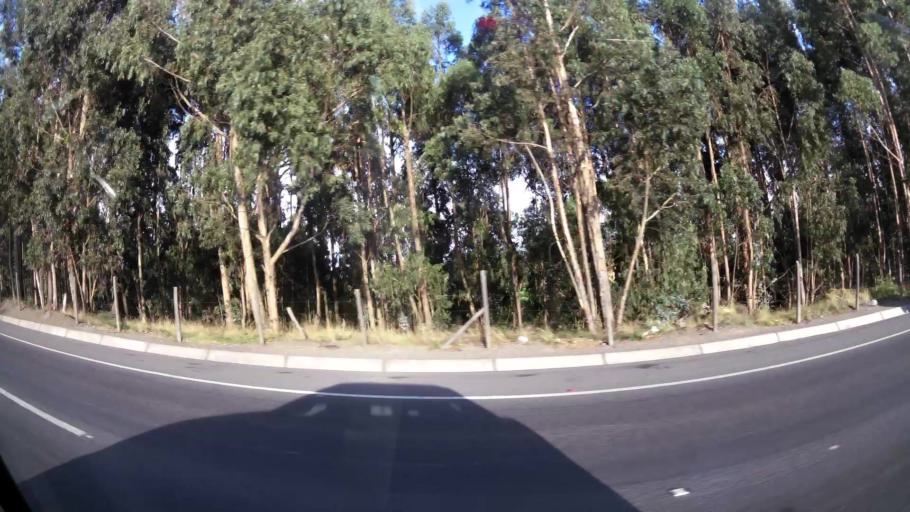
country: EC
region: Cotopaxi
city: Saquisili
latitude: -0.8381
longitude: -78.6192
